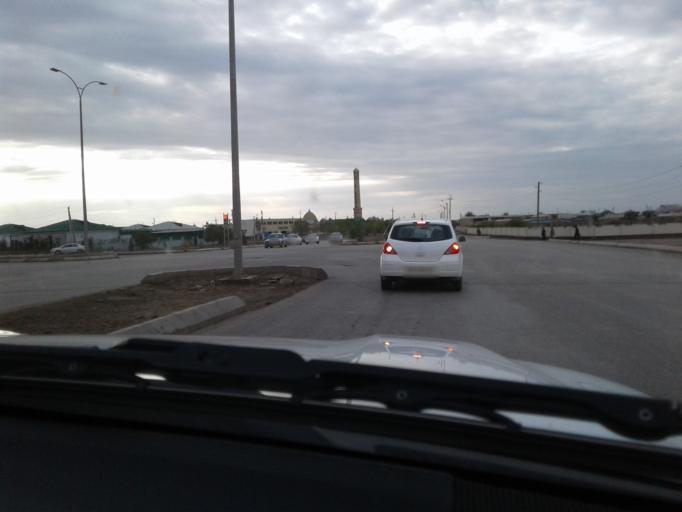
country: TM
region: Ahal
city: Tejen
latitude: 37.3753
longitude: 60.5178
